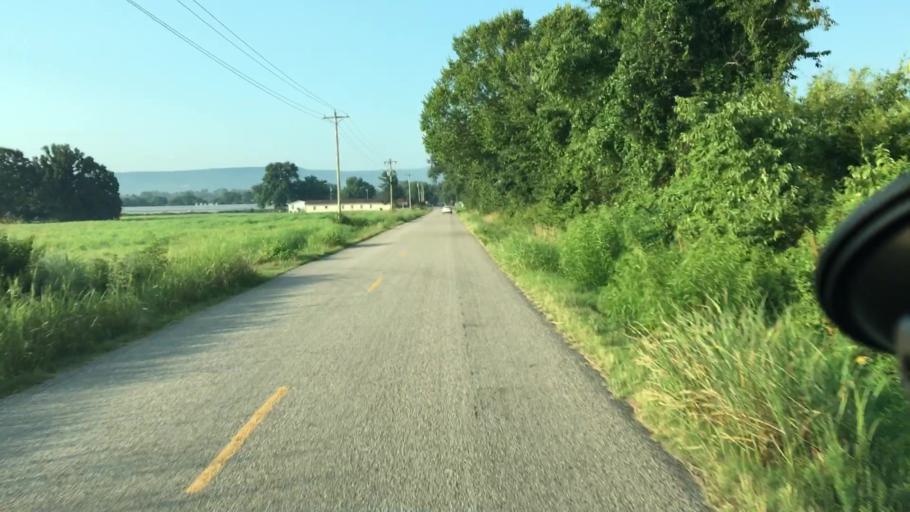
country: US
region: Arkansas
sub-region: Johnson County
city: Coal Hill
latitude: 35.3404
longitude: -93.6137
